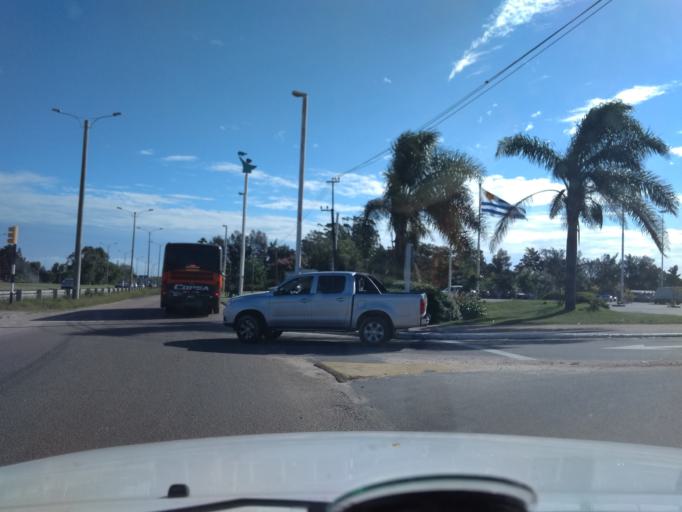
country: UY
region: Canelones
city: Barra de Carrasco
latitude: -34.8668
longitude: -56.0223
